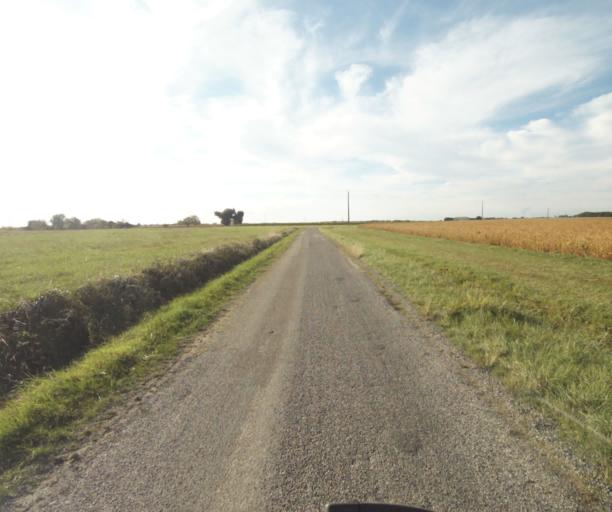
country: FR
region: Midi-Pyrenees
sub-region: Departement du Tarn-et-Garonne
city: Finhan
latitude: 43.9049
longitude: 1.1320
